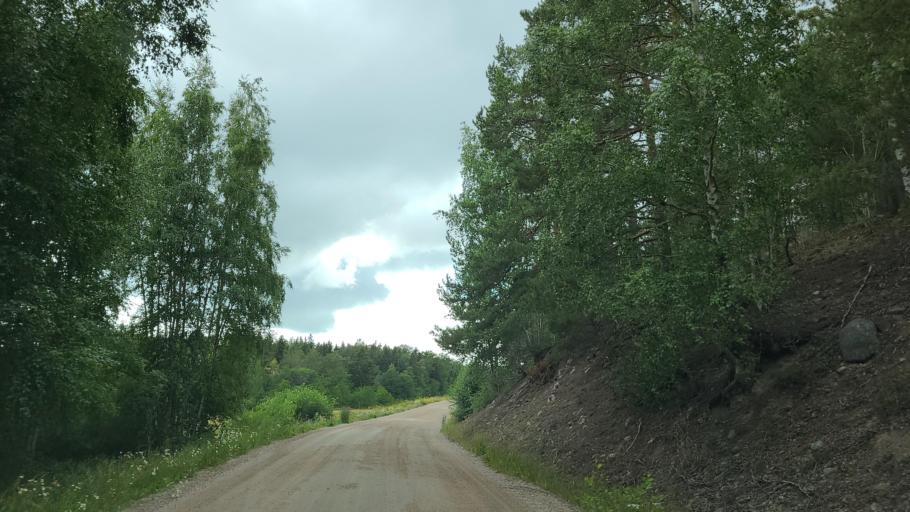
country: FI
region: Varsinais-Suomi
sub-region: Aboland-Turunmaa
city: Nagu
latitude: 60.2055
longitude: 21.8447
